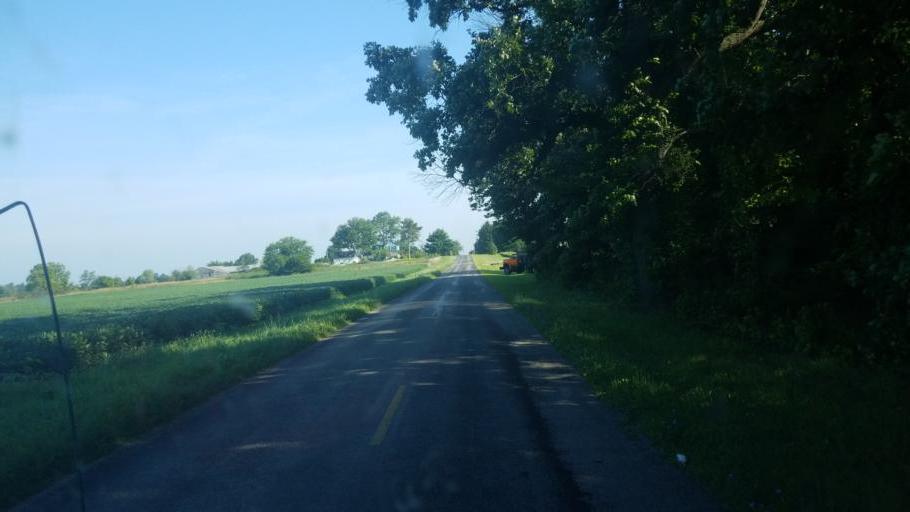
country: US
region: Ohio
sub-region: Huron County
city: New London
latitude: 41.0709
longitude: -82.3469
